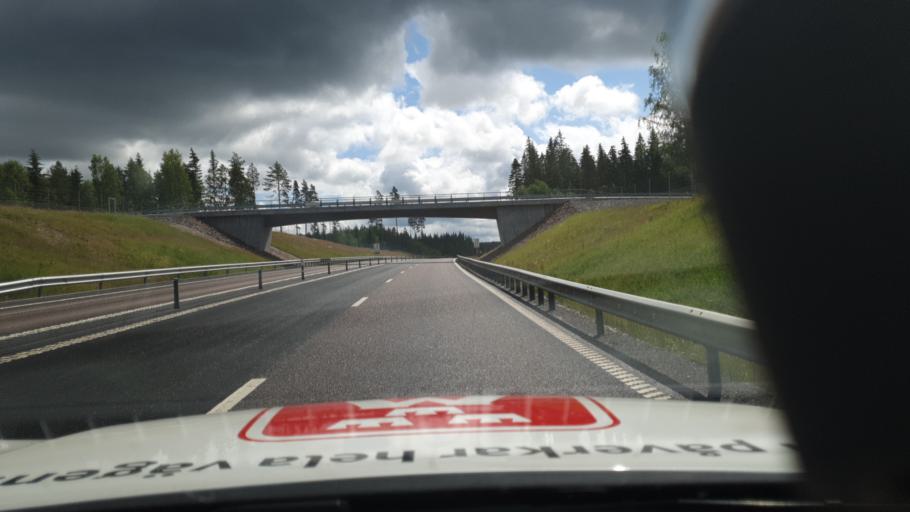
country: SE
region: Joenkoeping
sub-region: Mullsjo Kommun
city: Mullsjoe
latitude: 57.8949
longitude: 13.8800
